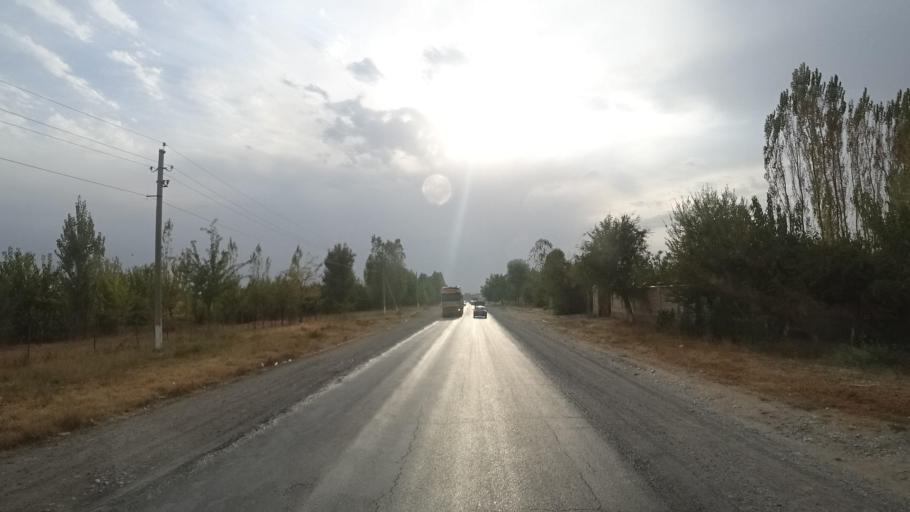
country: KG
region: Jalal-Abad
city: Massy
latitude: 41.0648
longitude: 72.6531
